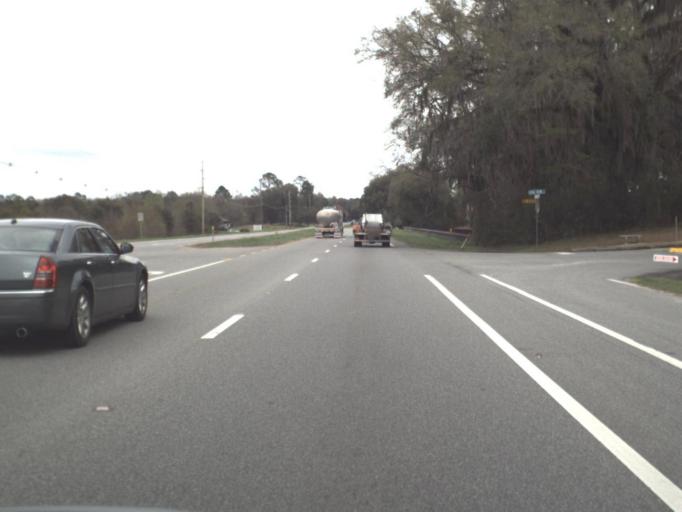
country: US
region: Florida
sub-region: Gadsden County
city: Midway
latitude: 30.5236
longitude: -84.3537
